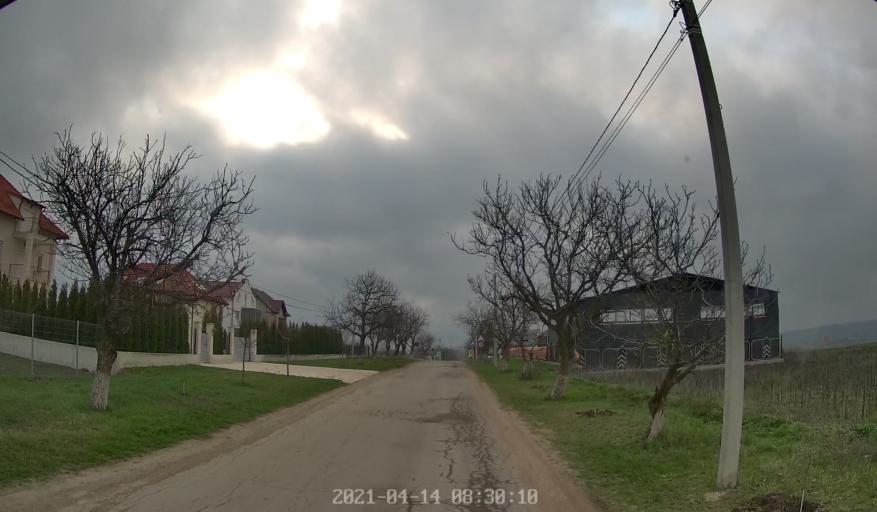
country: MD
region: Chisinau
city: Stauceni
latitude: 47.0631
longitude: 28.9273
